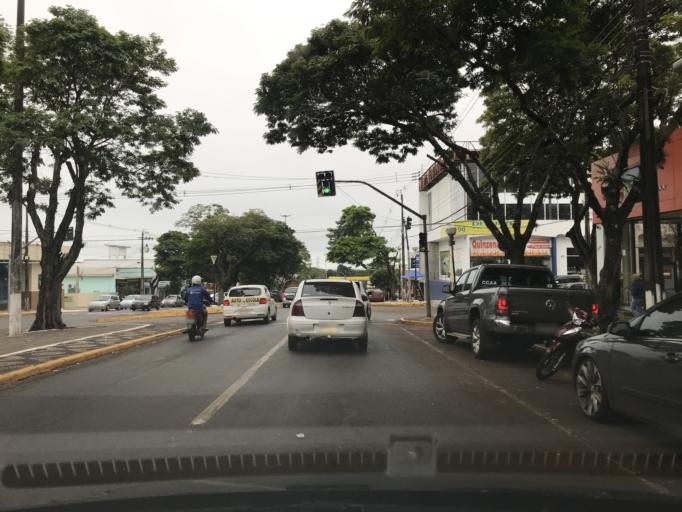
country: PY
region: Canindeyu
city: Salto del Guaira
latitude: -24.0818
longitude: -54.2553
